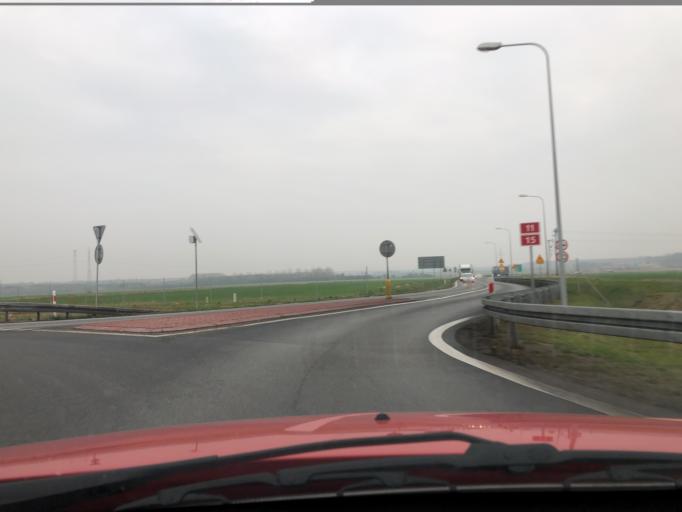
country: PL
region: Greater Poland Voivodeship
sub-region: Powiat jarocinski
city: Jarocin
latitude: 51.9771
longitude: 17.5234
